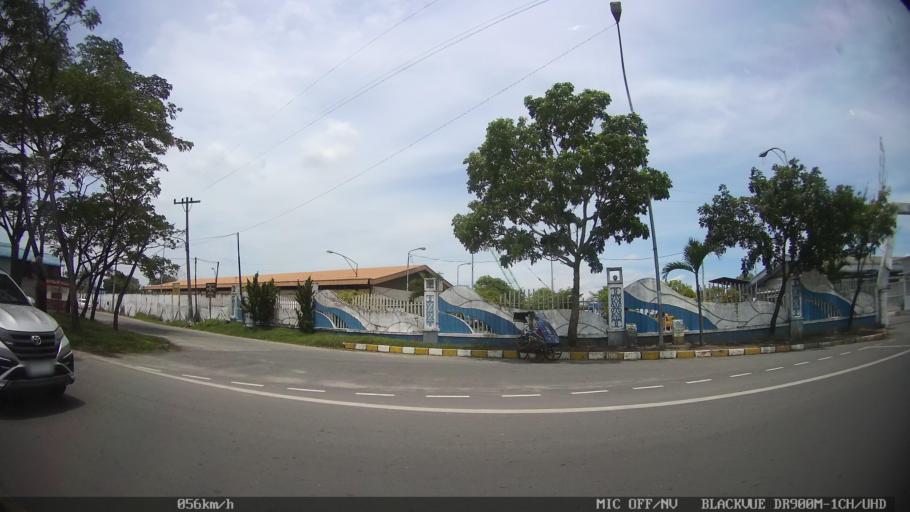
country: ID
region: North Sumatra
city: Belawan
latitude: 3.7778
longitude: 98.6812
